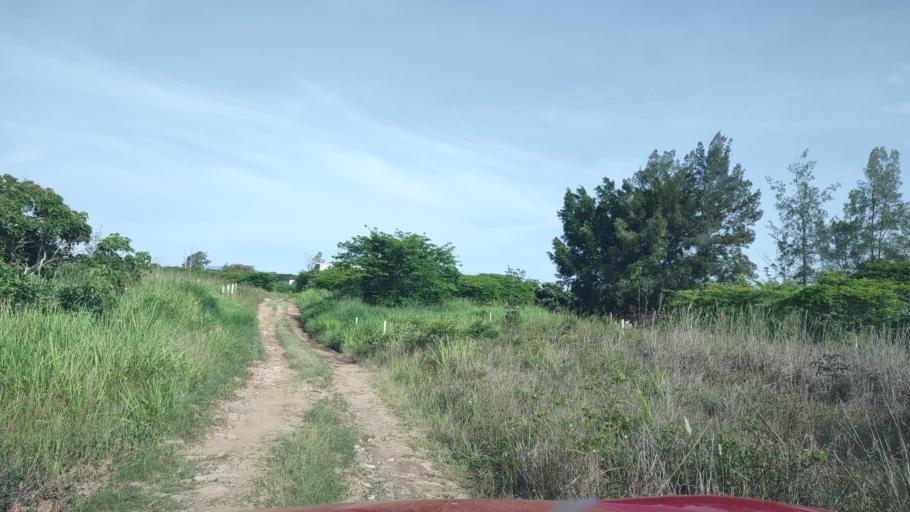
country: MX
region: Veracruz
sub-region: Emiliano Zapata
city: Dos Rios
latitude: 19.4755
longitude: -96.8267
